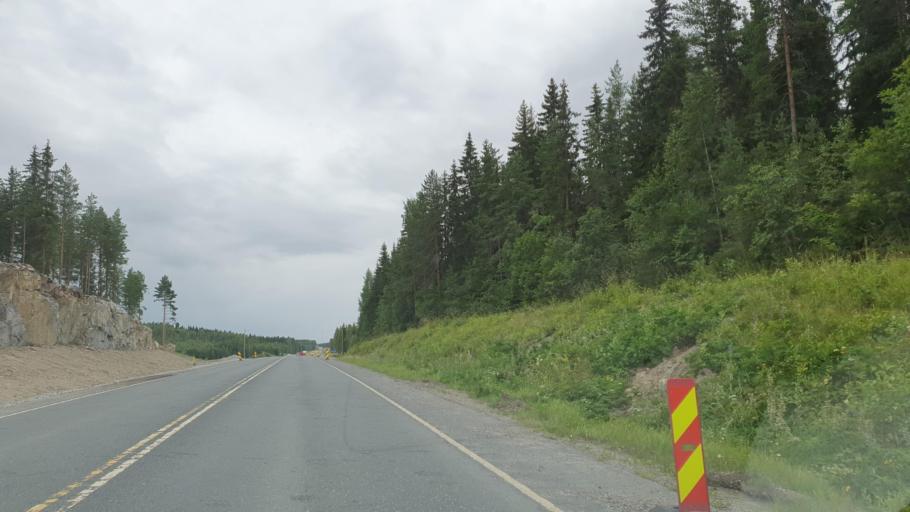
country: FI
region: Northern Savo
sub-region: Ylae-Savo
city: Lapinlahti
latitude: 63.3054
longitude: 27.4502
